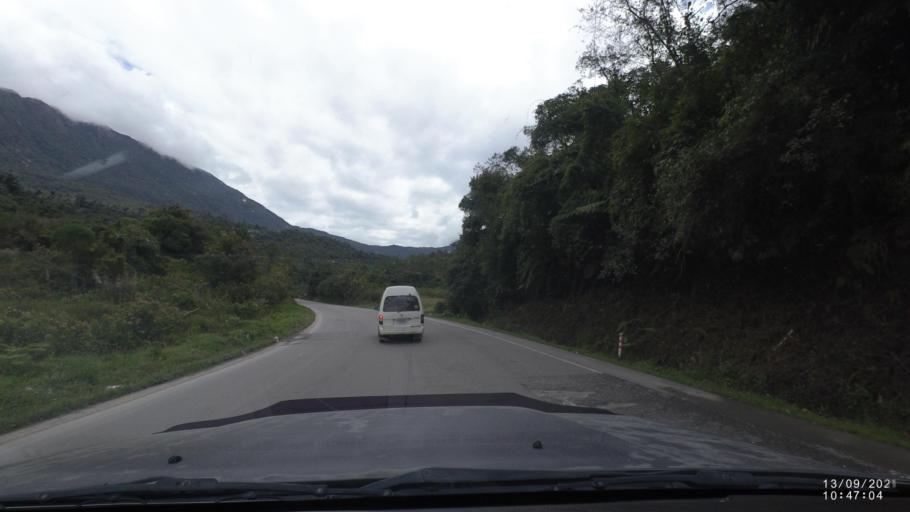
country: BO
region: Cochabamba
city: Colomi
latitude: -17.2020
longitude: -65.8623
